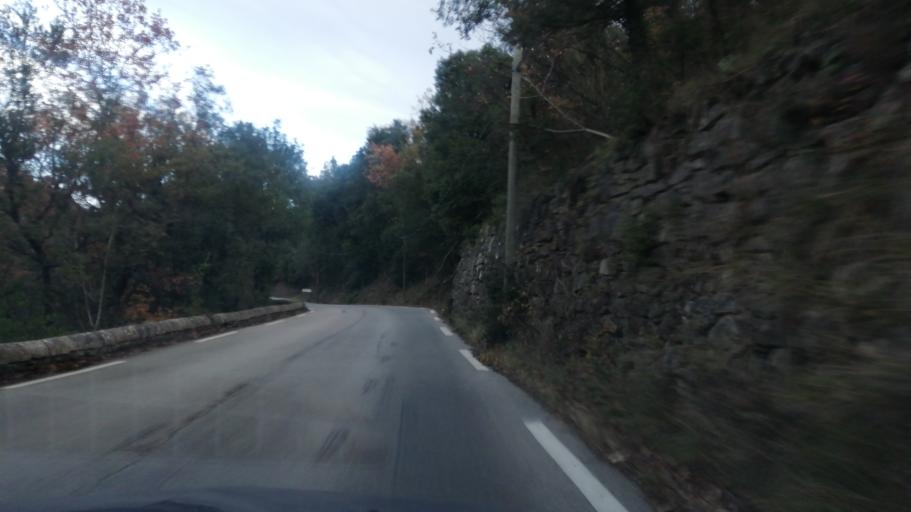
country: FR
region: Languedoc-Roussillon
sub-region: Departement du Gard
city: Saint-Hippolyte-du-Fort
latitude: 43.9831
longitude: 3.8527
